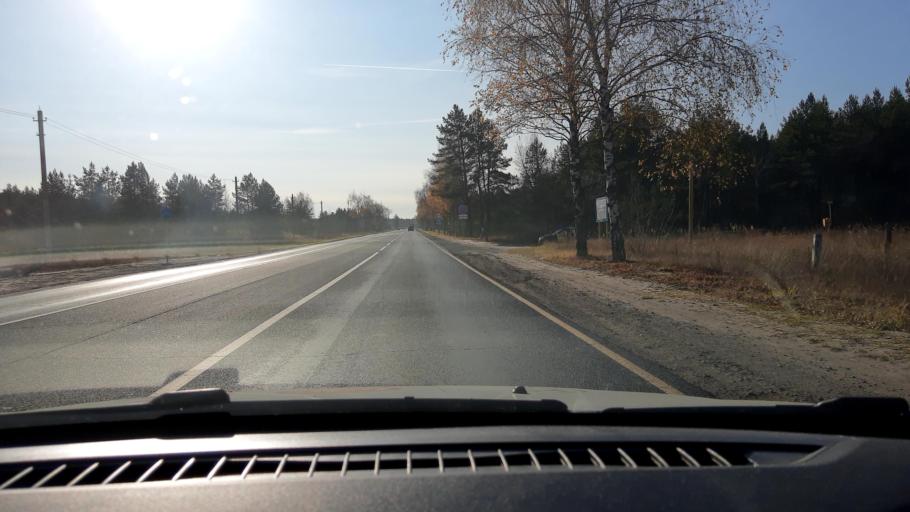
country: RU
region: Nizjnij Novgorod
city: Dzerzhinsk
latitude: 56.2846
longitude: 43.4755
